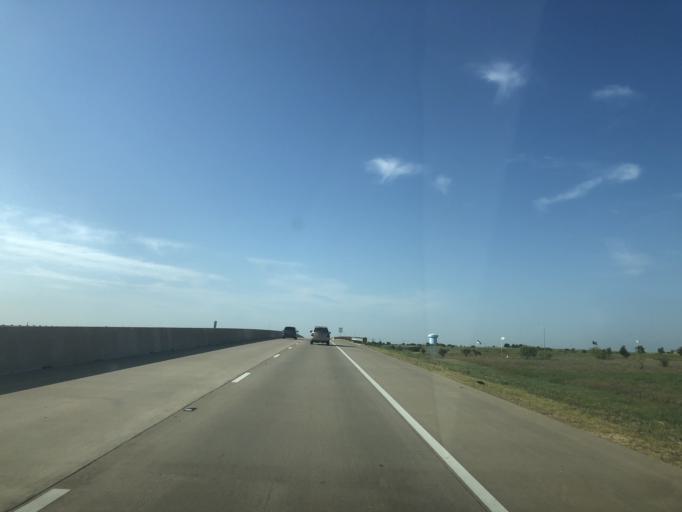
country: US
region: Texas
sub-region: Tarrant County
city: Crowley
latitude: 32.6175
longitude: -97.4127
